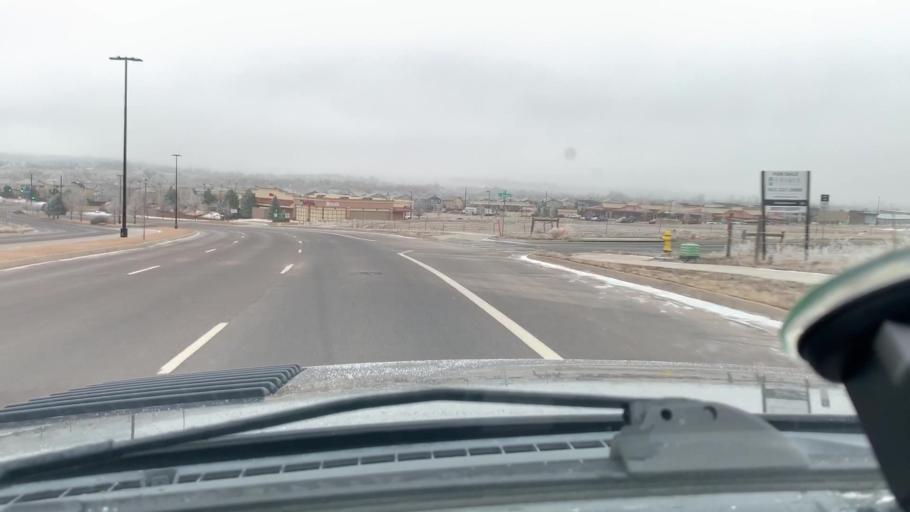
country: US
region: Colorado
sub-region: Arapahoe County
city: Dove Valley
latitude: 39.5757
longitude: -104.8106
